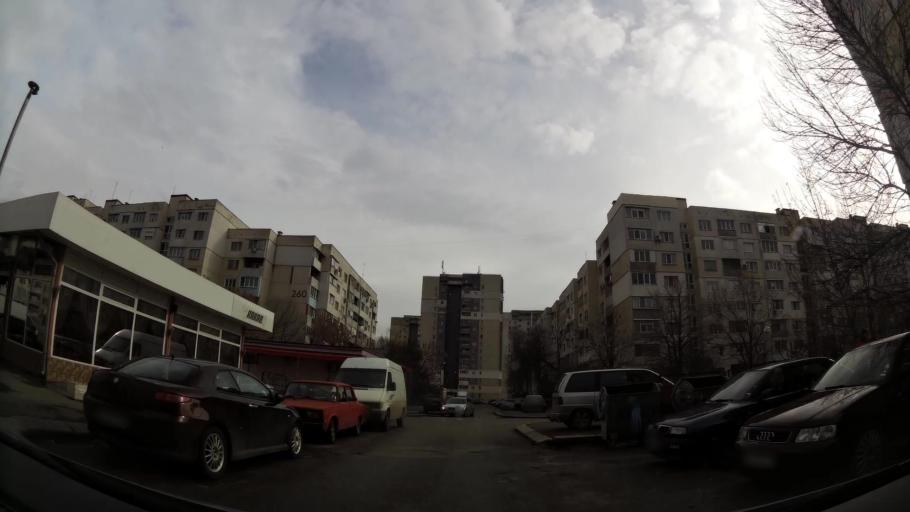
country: BG
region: Sofia-Capital
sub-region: Stolichna Obshtina
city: Sofia
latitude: 42.7452
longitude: 23.2794
